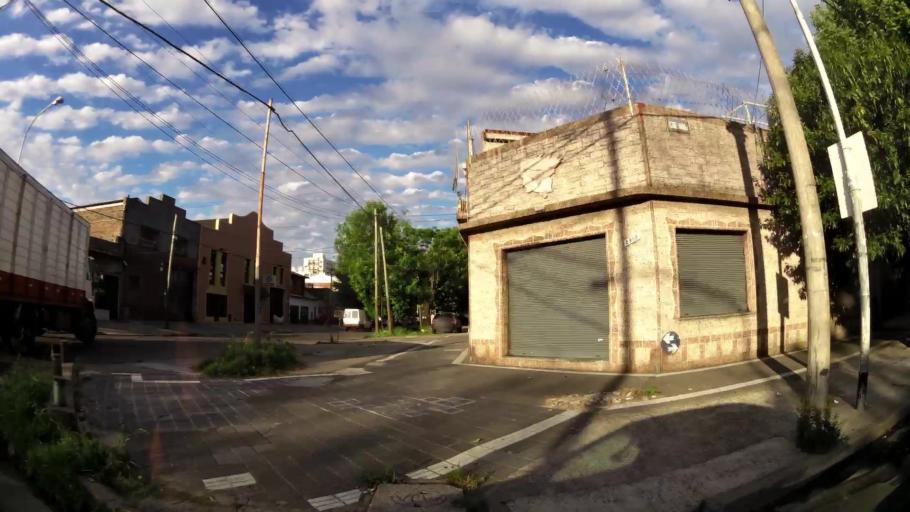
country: AR
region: Buenos Aires
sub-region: Partido de Avellaneda
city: Avellaneda
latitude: -34.6811
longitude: -58.3487
